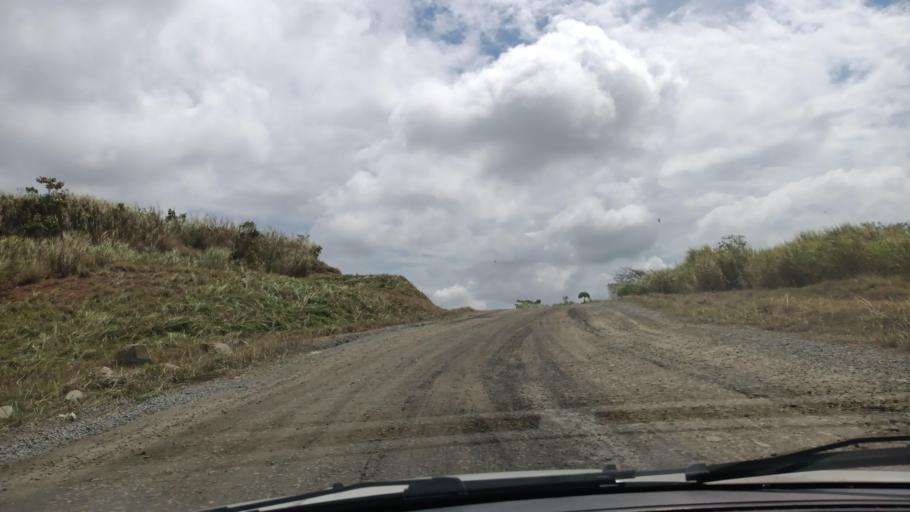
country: PA
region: Panama
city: Las Cumbres
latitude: 9.1054
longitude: -79.4995
